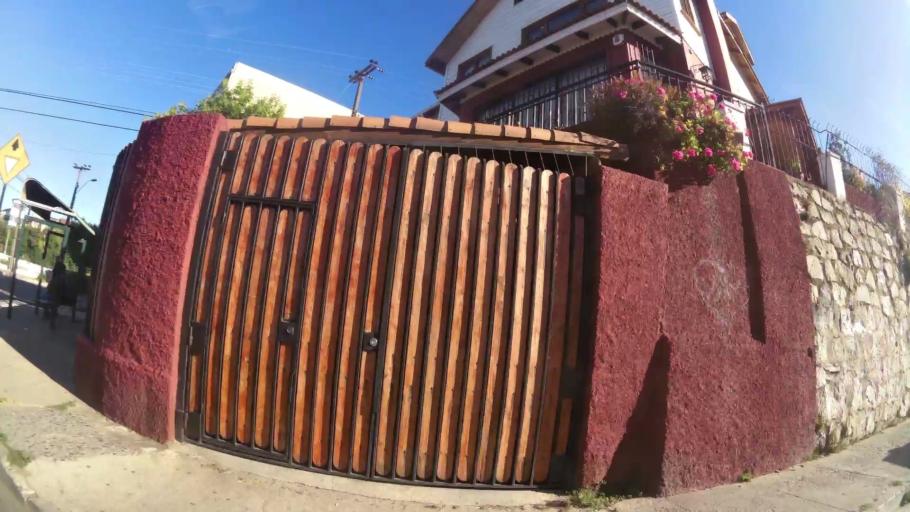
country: CL
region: Valparaiso
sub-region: Provincia de Valparaiso
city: Valparaiso
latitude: -33.0533
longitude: -71.6260
